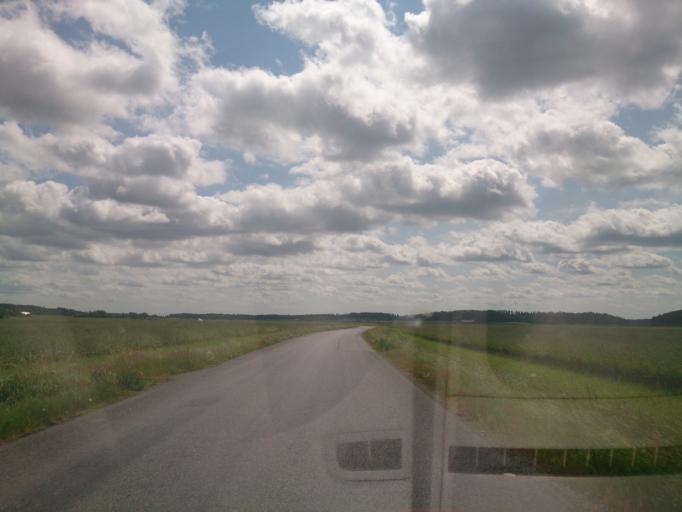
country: SE
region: OEstergoetland
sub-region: Norrkopings Kommun
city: Krokek
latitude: 58.5223
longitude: 16.4889
